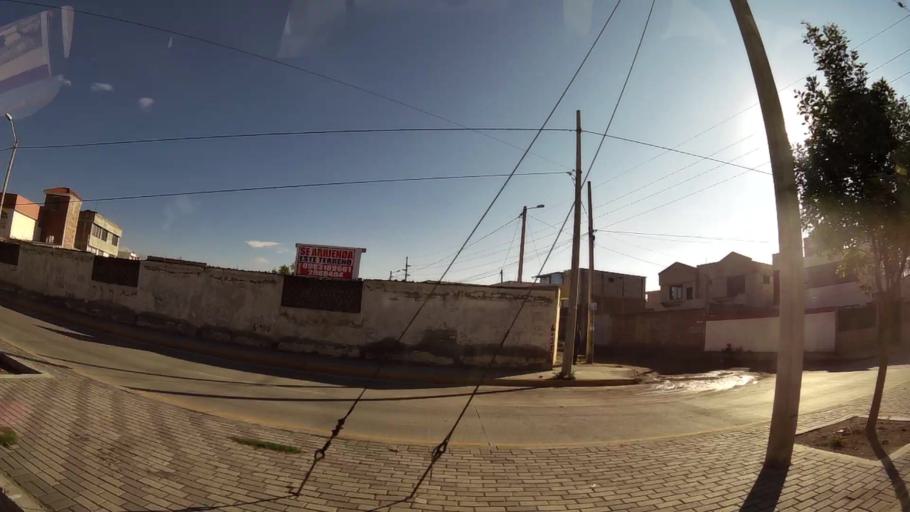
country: EC
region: Chimborazo
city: Riobamba
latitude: -1.6757
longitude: -78.6305
